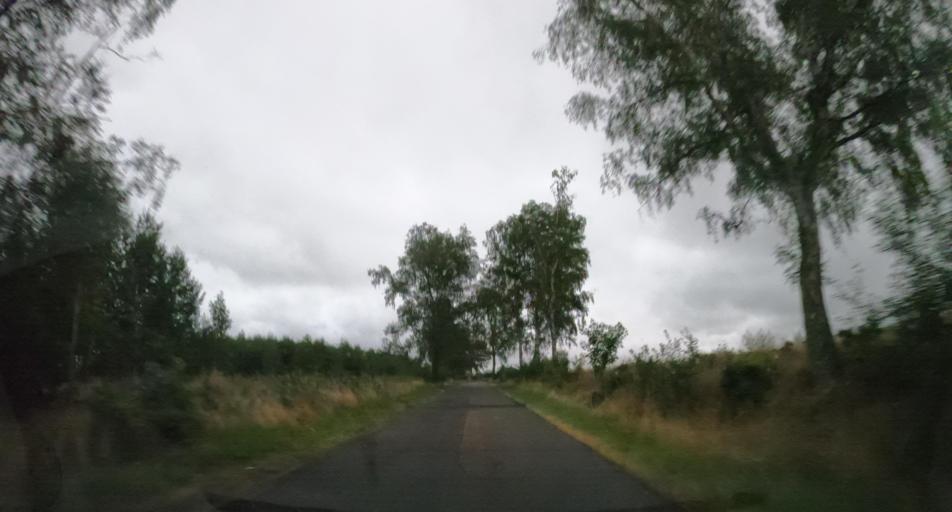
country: PL
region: West Pomeranian Voivodeship
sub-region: Powiat lobeski
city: Resko
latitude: 53.7565
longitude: 15.4304
